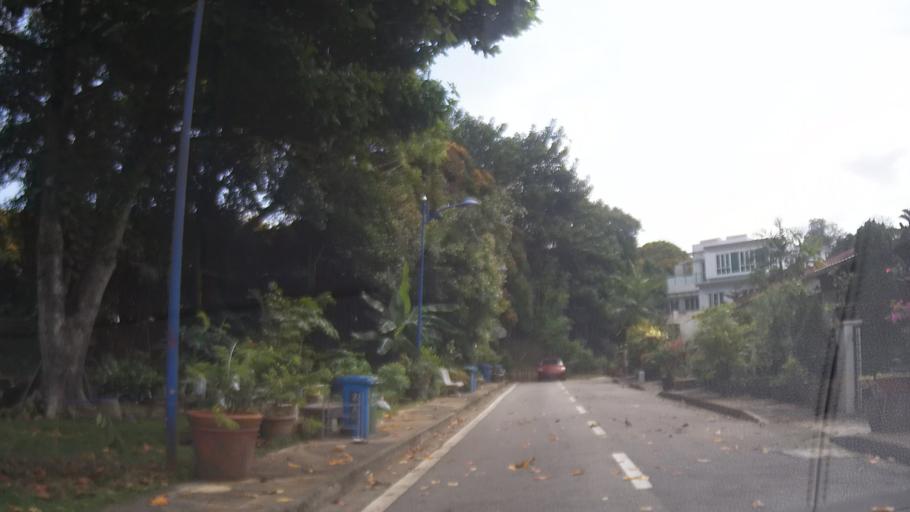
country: MY
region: Johor
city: Johor Bahru
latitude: 1.4174
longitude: 103.7597
